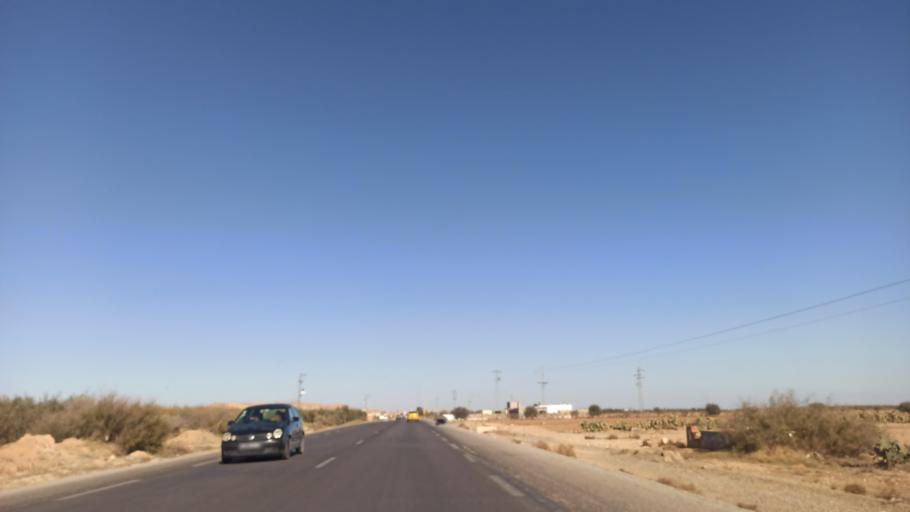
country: TN
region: Sidi Bu Zayd
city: Bi'r al Hufayy
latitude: 34.9016
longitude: 9.1757
